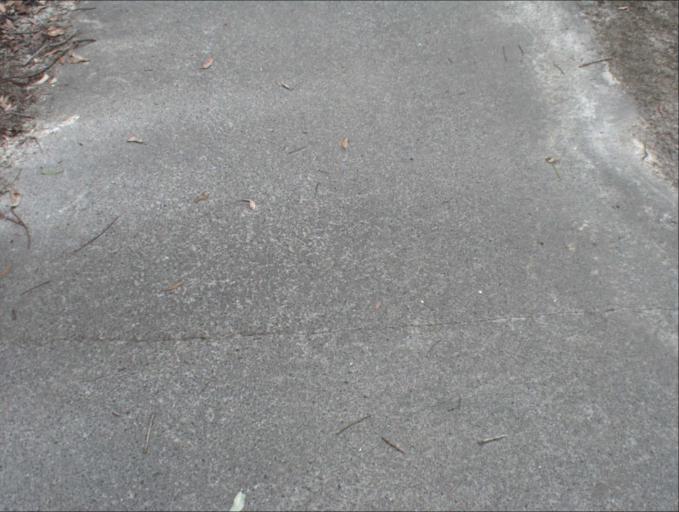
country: AU
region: Queensland
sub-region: Logan
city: Beenleigh
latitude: -27.6584
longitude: 153.2079
